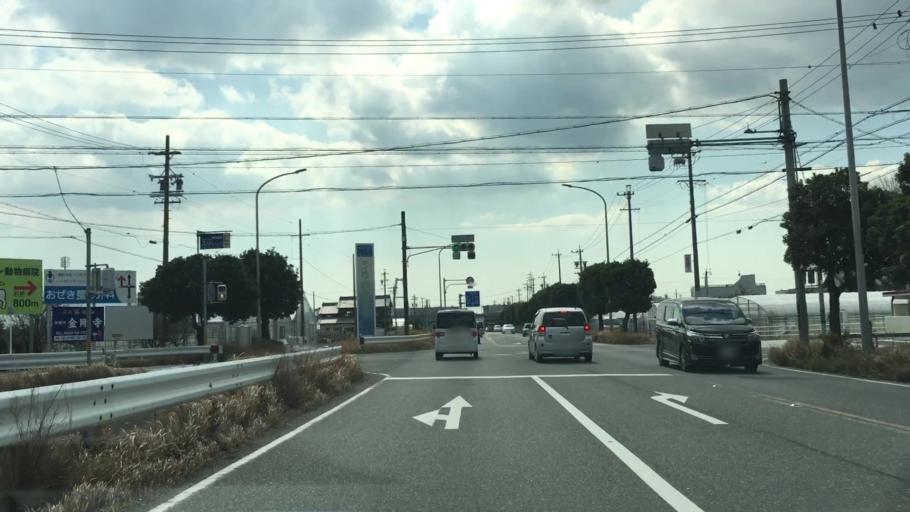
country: JP
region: Aichi
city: Kozakai-cho
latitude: 34.8119
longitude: 137.3111
